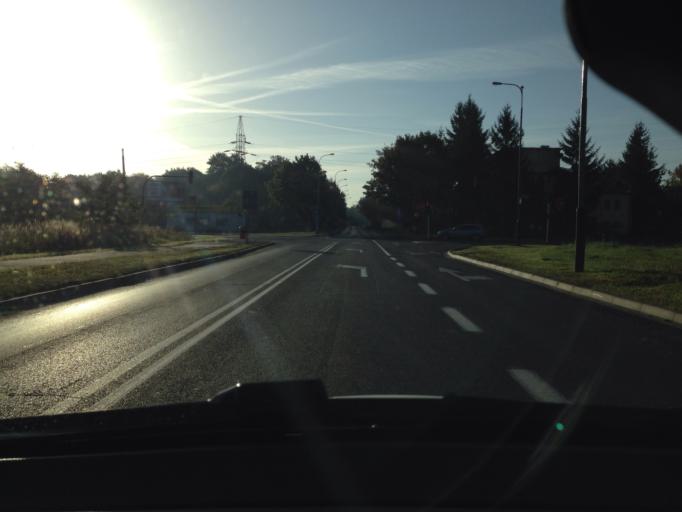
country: PL
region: Greater Poland Voivodeship
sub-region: Powiat poznanski
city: Suchy Las
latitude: 52.4429
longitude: 16.9046
